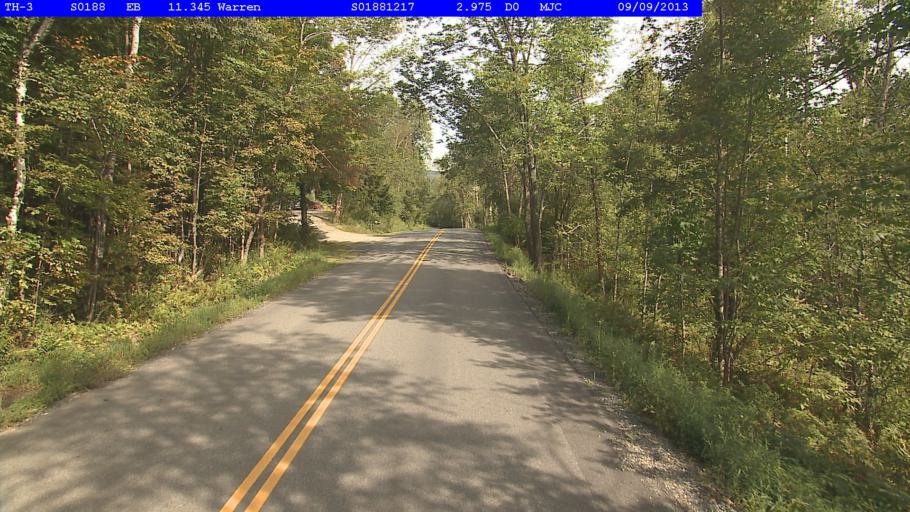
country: US
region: Vermont
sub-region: Addison County
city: Bristol
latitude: 44.1041
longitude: -72.8735
